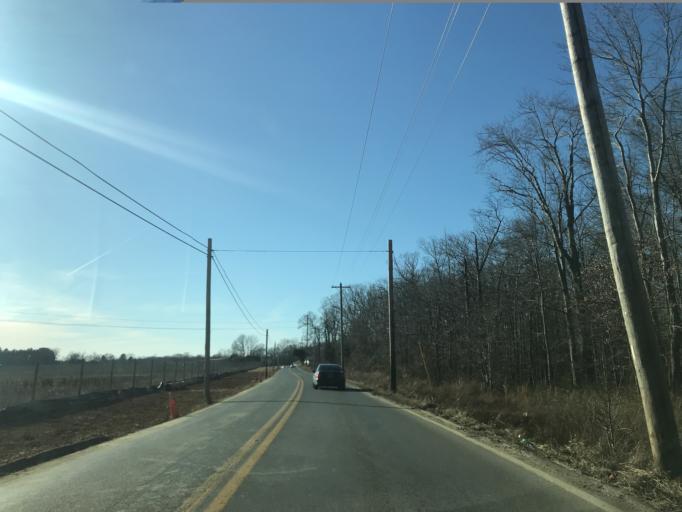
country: US
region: Maryland
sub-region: Charles County
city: Waldorf
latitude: 38.6742
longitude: -76.9670
